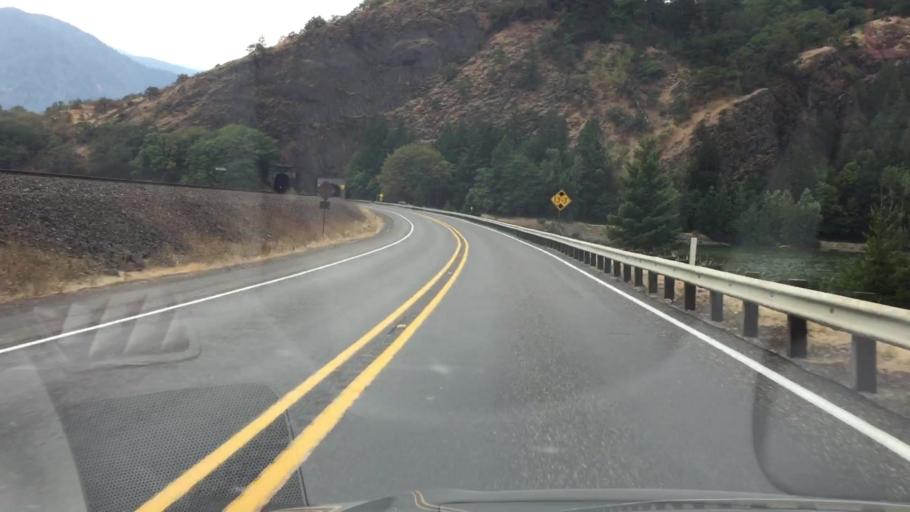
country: US
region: Oregon
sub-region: Hood River County
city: Hood River
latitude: 45.7171
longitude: -121.6146
